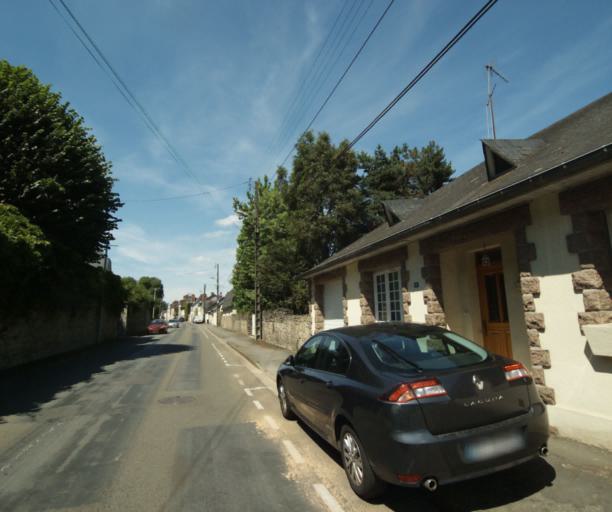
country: FR
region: Pays de la Loire
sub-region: Departement de la Mayenne
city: Laval
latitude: 48.0815
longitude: -0.7724
